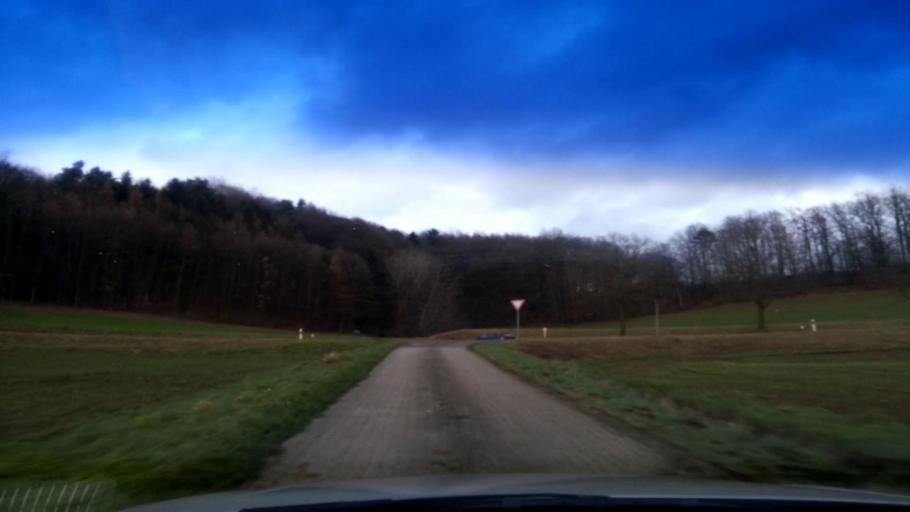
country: DE
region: Bavaria
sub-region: Upper Franconia
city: Schesslitz
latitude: 50.0110
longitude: 11.0331
